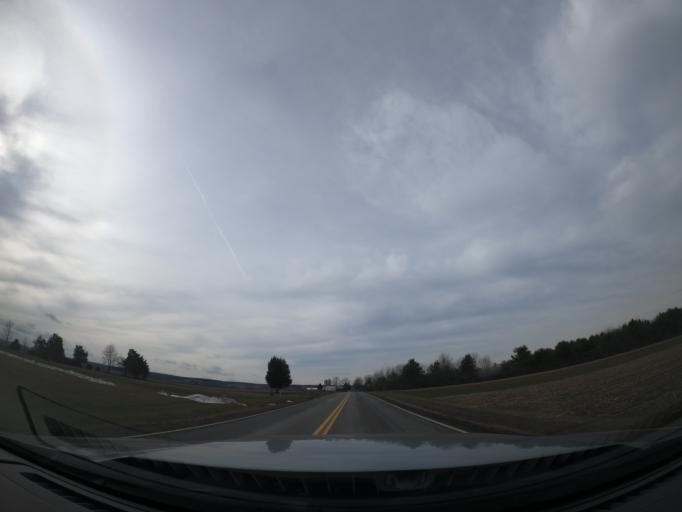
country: US
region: New York
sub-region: Yates County
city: Dundee
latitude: 42.4994
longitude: -76.9471
